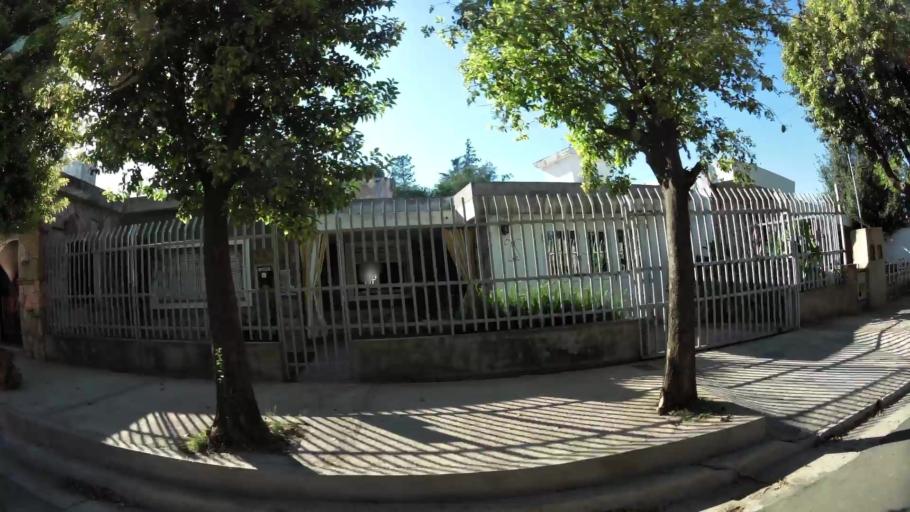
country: AR
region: Cordoba
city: Villa Allende
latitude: -31.3283
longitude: -64.2602
